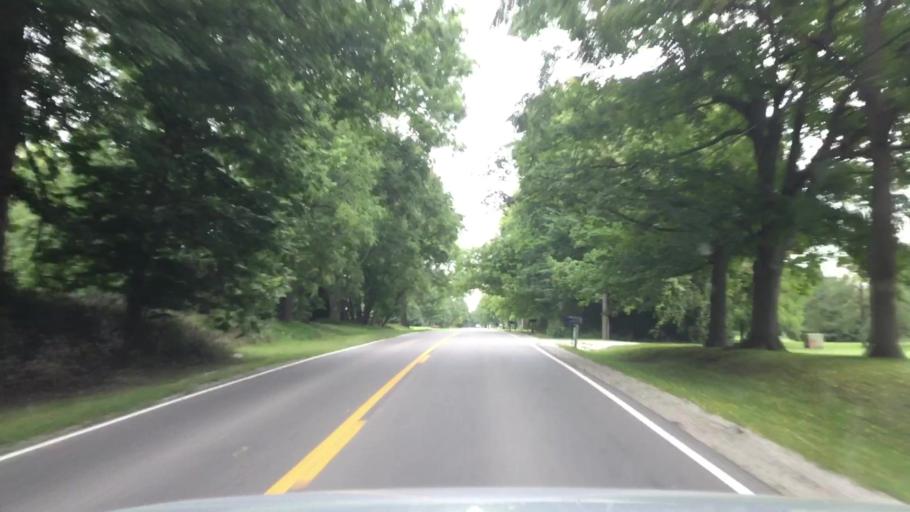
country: US
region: Michigan
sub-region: Washtenaw County
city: Ypsilanti
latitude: 42.1815
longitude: -83.6389
